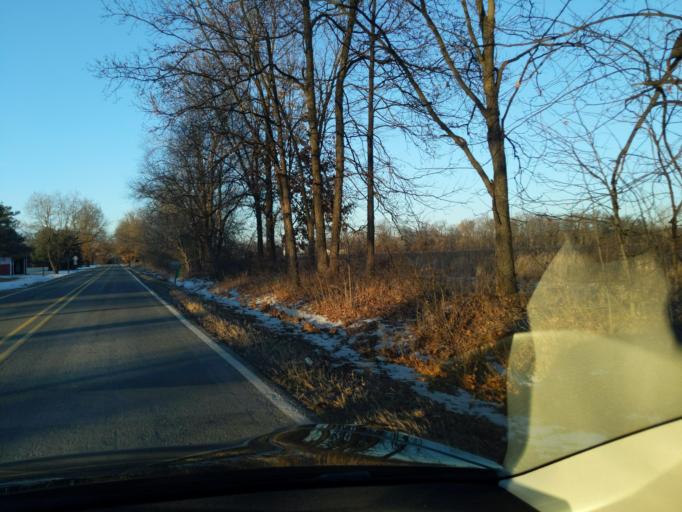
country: US
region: Michigan
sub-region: Ingham County
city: Stockbridge
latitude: 42.4874
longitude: -84.2177
